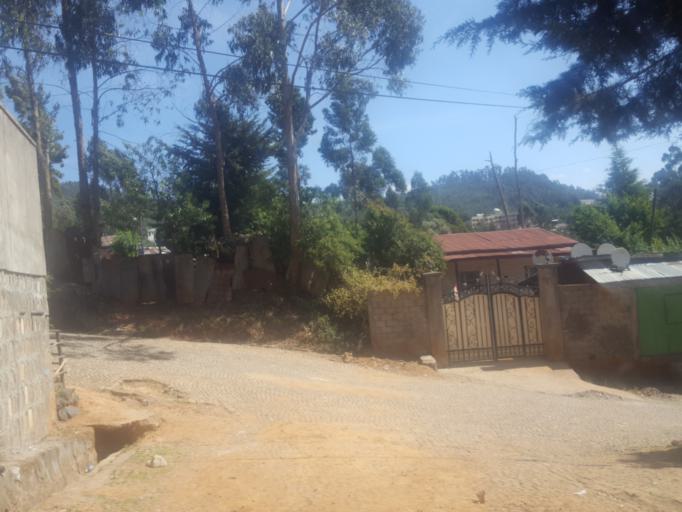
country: ET
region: Adis Abeba
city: Addis Ababa
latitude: 9.0703
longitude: 38.7321
